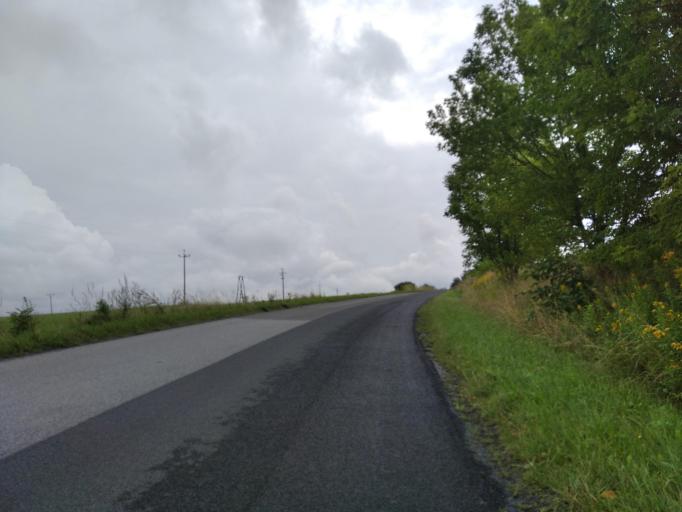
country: PL
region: Subcarpathian Voivodeship
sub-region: Powiat rzeszowski
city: Dynow
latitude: 49.7211
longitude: 22.3169
